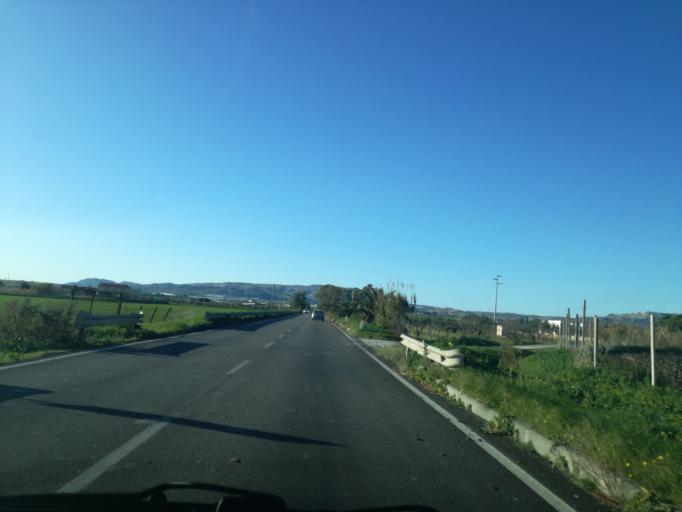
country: IT
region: Sicily
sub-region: Provincia di Caltanissetta
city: Butera
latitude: 37.1166
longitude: 14.1412
